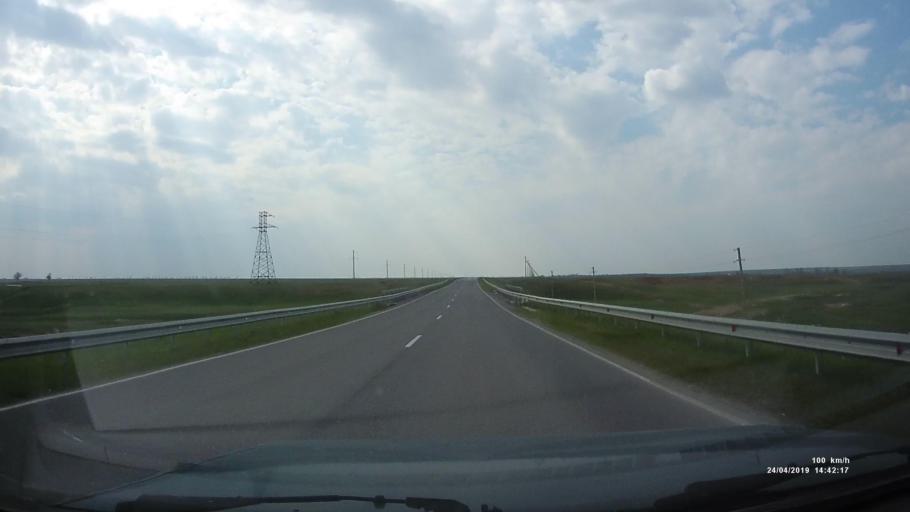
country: RU
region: Rostov
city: Remontnoye
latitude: 46.4512
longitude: 43.8651
